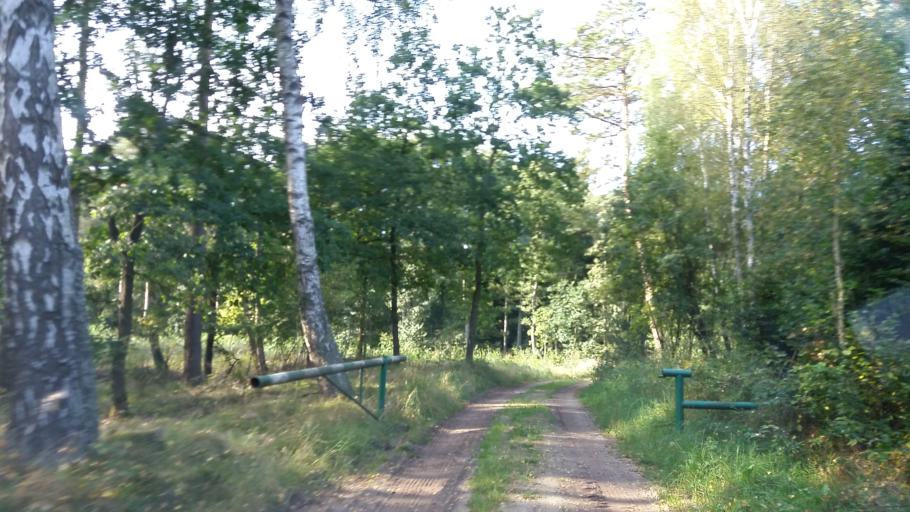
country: PL
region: West Pomeranian Voivodeship
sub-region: Powiat stargardzki
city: Suchan
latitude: 53.2435
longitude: 15.3944
